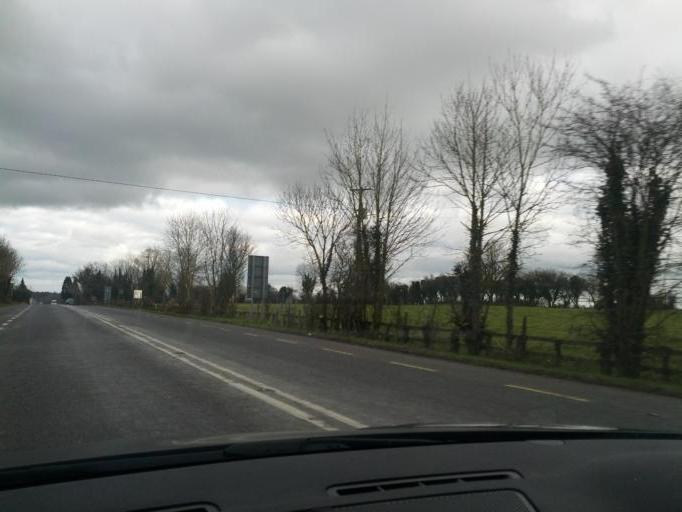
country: IE
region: Leinster
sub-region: An Iarmhi
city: Moate
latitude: 53.3957
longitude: -7.6979
